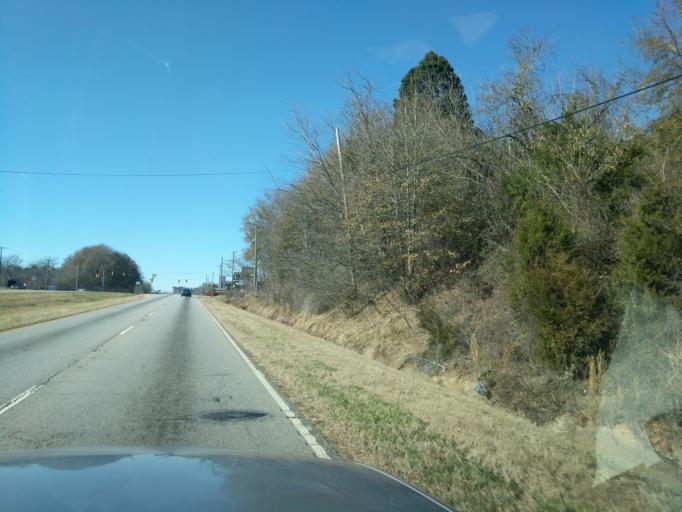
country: US
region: South Carolina
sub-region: Anderson County
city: Powdersville
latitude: 34.8301
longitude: -82.5150
